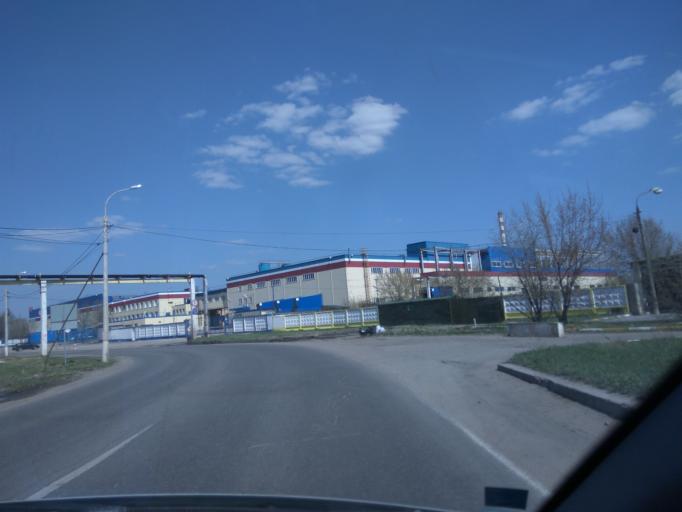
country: RU
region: Moskovskaya
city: Ramenskoye
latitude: 55.5611
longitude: 38.2633
